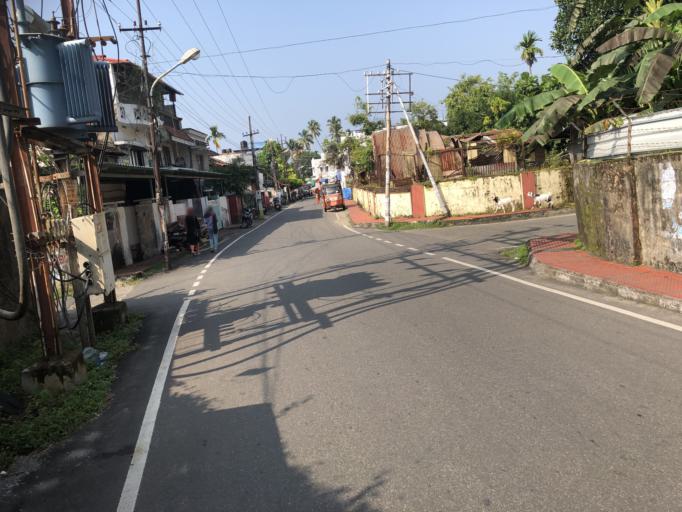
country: IN
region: Kerala
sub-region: Ernakulam
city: Cochin
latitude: 9.9590
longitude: 76.2532
